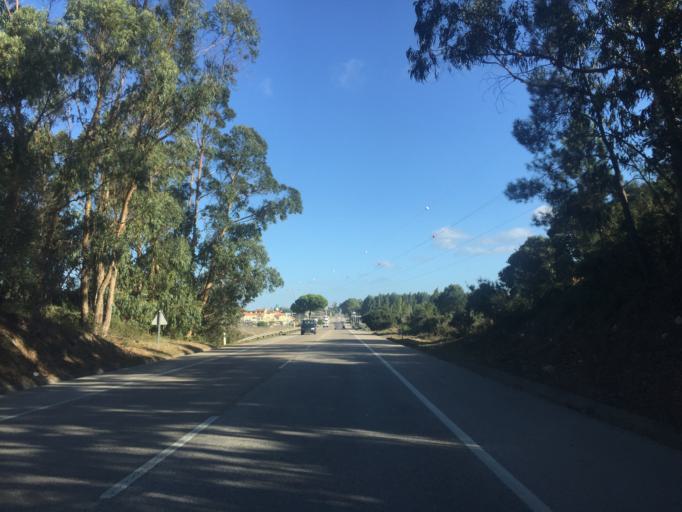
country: PT
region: Leiria
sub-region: Alcobaca
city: Turquel
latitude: 39.4587
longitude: -8.9462
